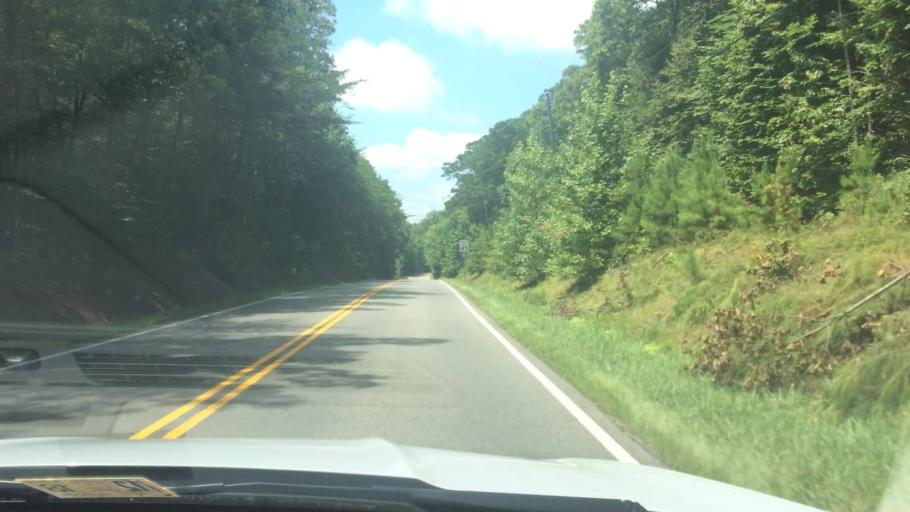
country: US
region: Virginia
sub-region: James City County
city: Williamsburg
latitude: 37.2798
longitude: -76.7831
